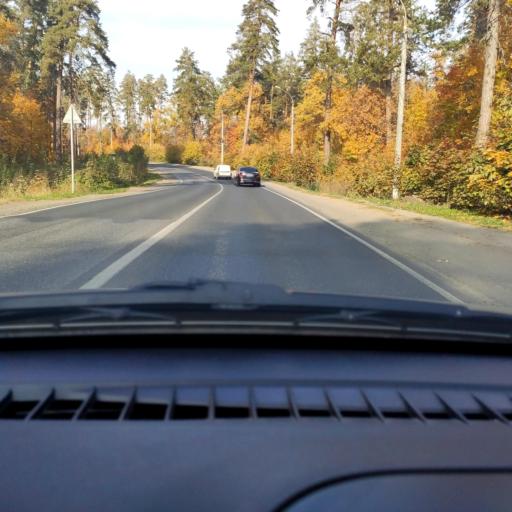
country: RU
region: Samara
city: Tol'yatti
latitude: 53.4898
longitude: 49.3068
